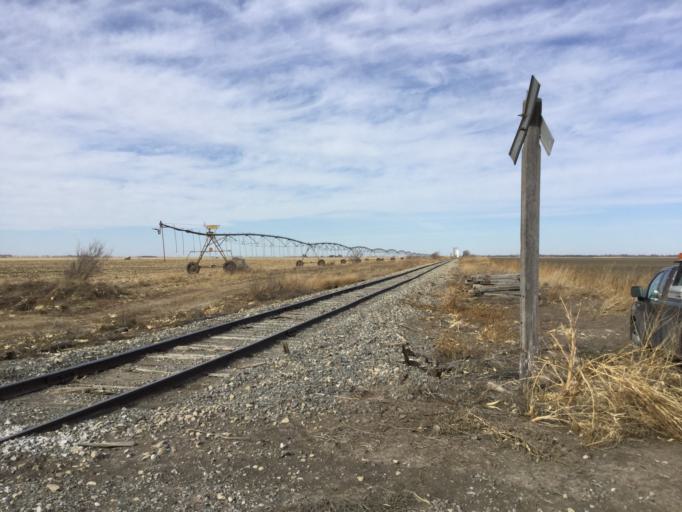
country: US
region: Kansas
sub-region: Pawnee County
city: Larned
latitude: 38.1723
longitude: -99.2775
